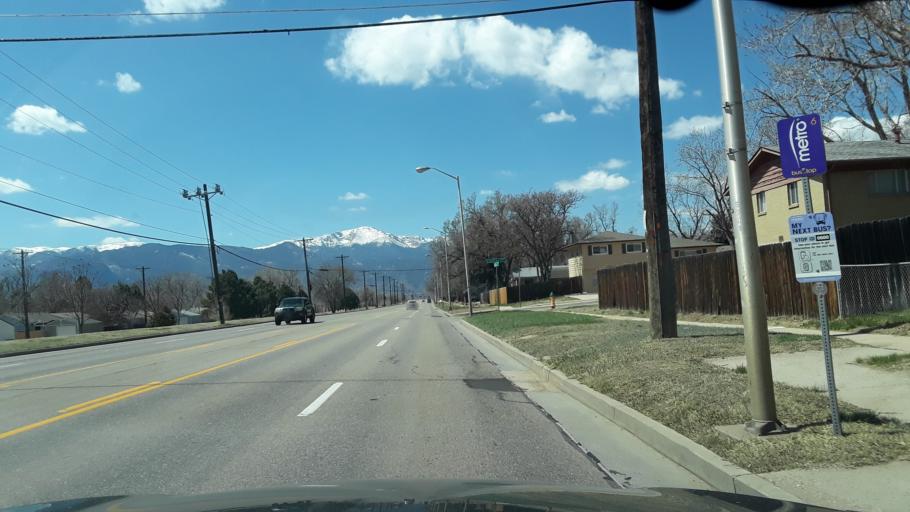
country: US
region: Colorado
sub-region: El Paso County
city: Colorado Springs
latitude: 38.8594
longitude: -104.7682
